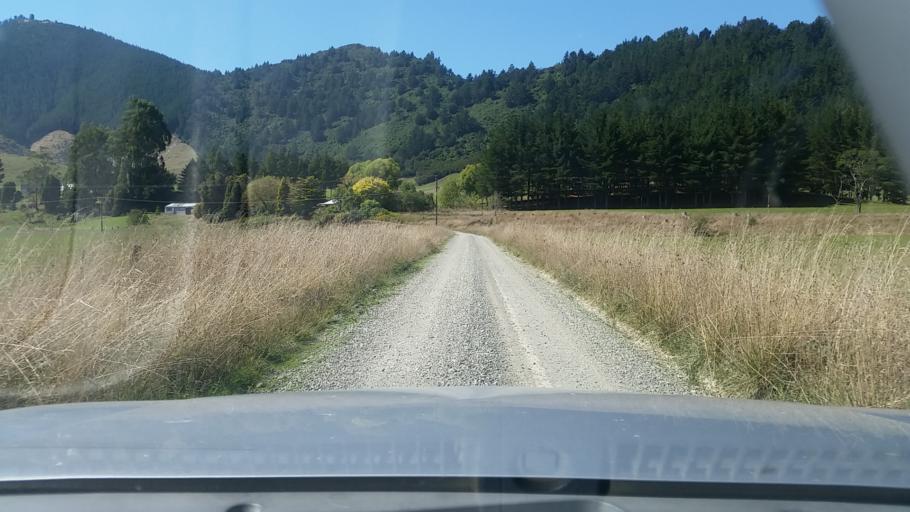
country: NZ
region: Nelson
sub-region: Nelson City
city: Nelson
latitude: -41.2604
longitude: 173.5782
